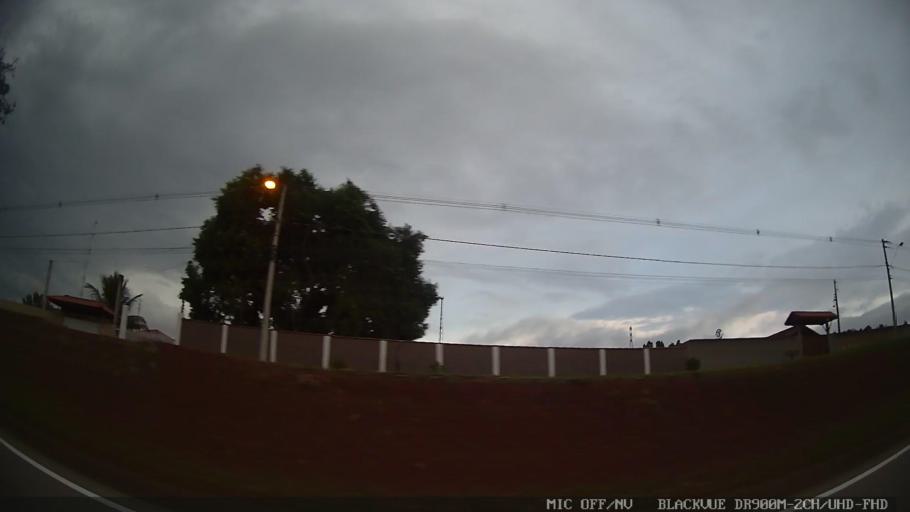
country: BR
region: Sao Paulo
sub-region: Caraguatatuba
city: Caraguatatuba
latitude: -23.4559
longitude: -45.5935
